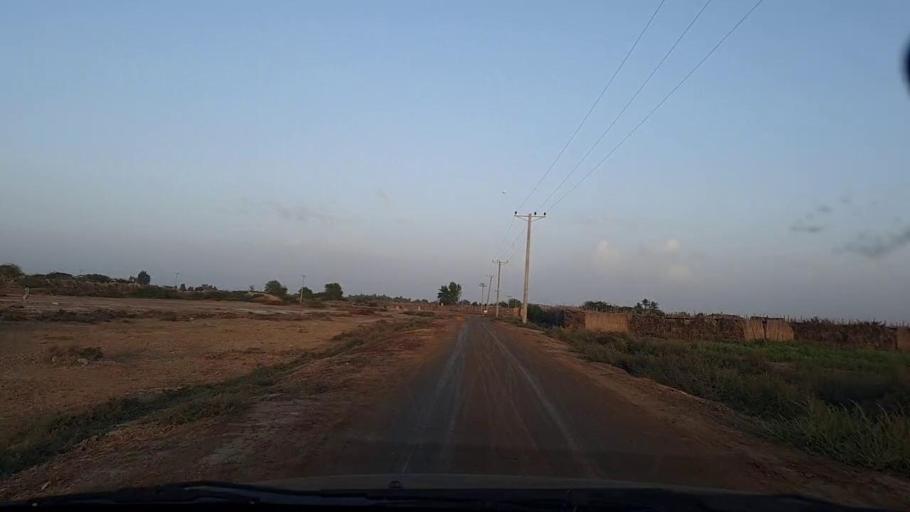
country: PK
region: Sindh
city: Keti Bandar
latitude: 24.1626
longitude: 67.6145
